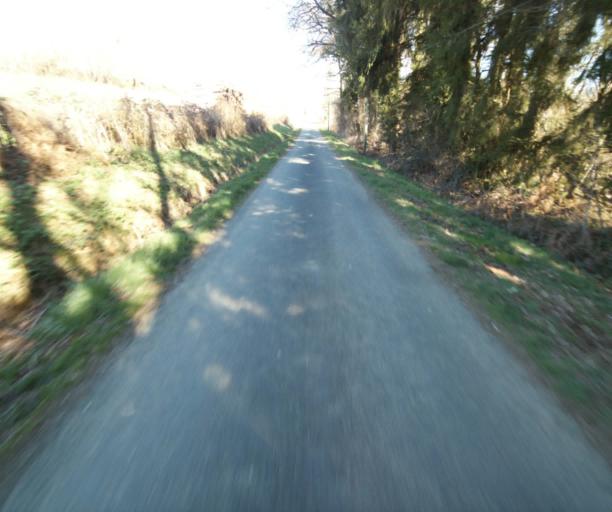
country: FR
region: Limousin
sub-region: Departement de la Correze
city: Chamboulive
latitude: 45.4145
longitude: 1.7218
